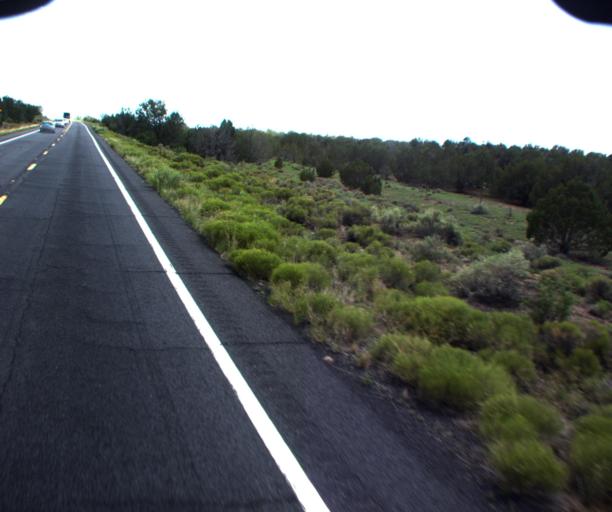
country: US
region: Arizona
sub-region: Coconino County
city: Williams
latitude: 35.5132
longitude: -112.1719
